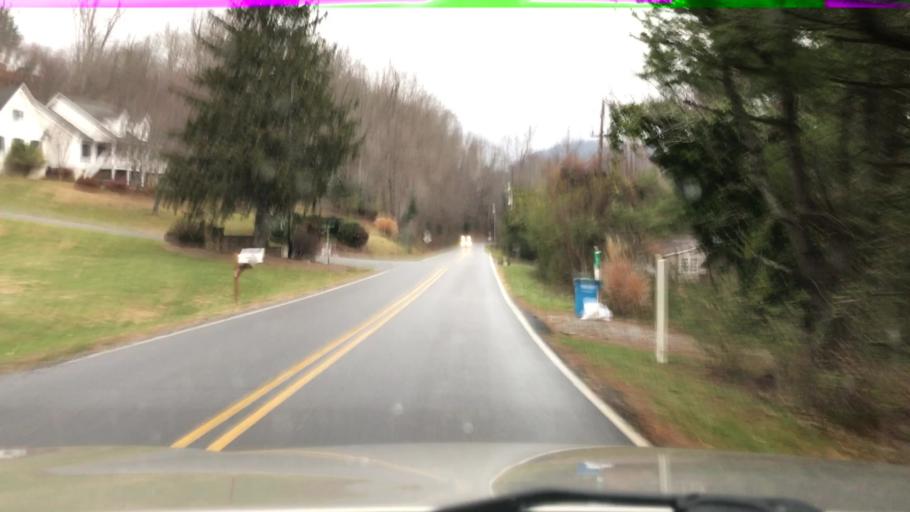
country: US
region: North Carolina
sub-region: Buncombe County
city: Avery Creek
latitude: 35.4748
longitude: -82.5580
